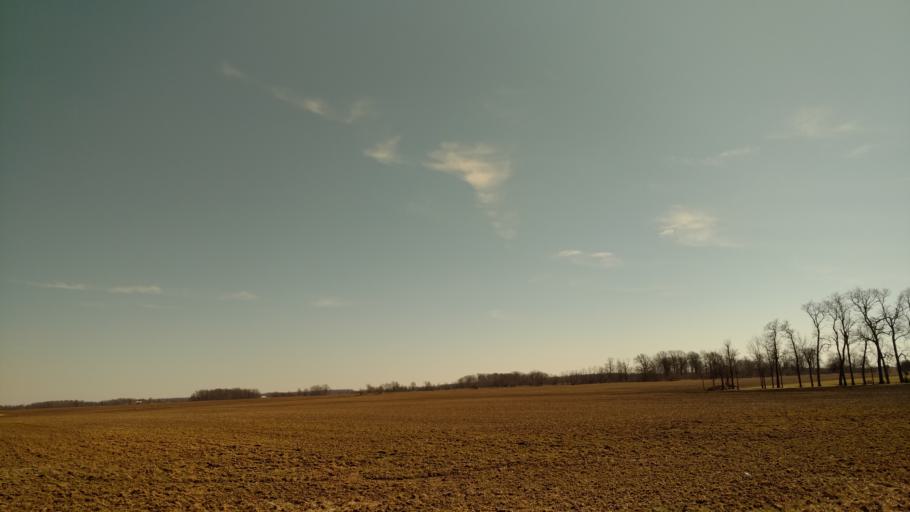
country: US
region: Ohio
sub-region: Union County
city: Richwood
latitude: 40.5314
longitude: -83.3144
